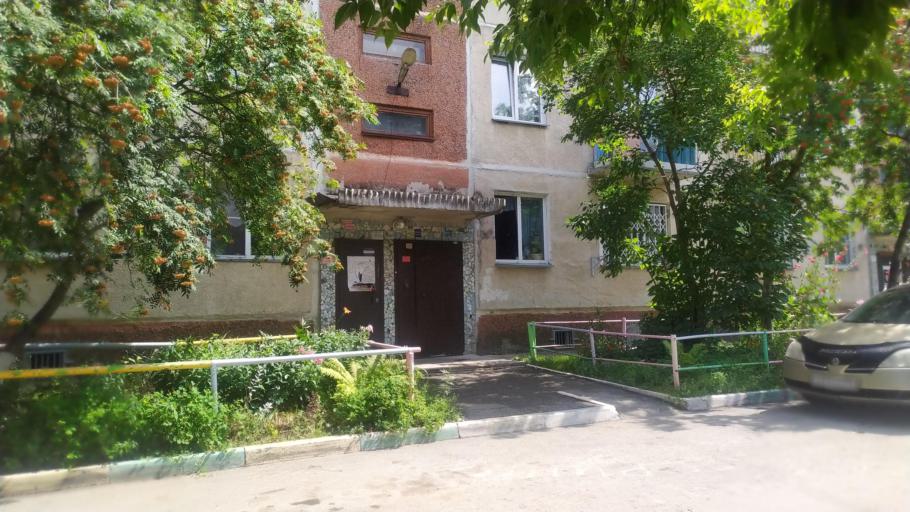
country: RU
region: Novosibirsk
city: Novolugovoye
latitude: 54.9388
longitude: 83.1260
